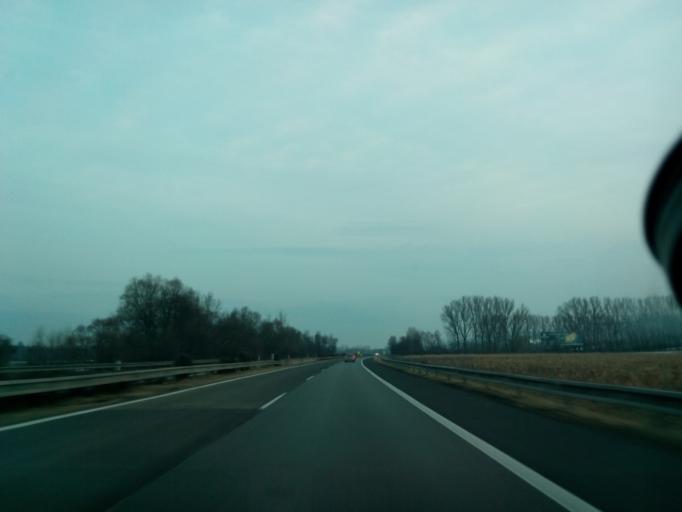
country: SK
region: Kosicky
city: Kosice
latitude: 48.7958
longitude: 21.3121
